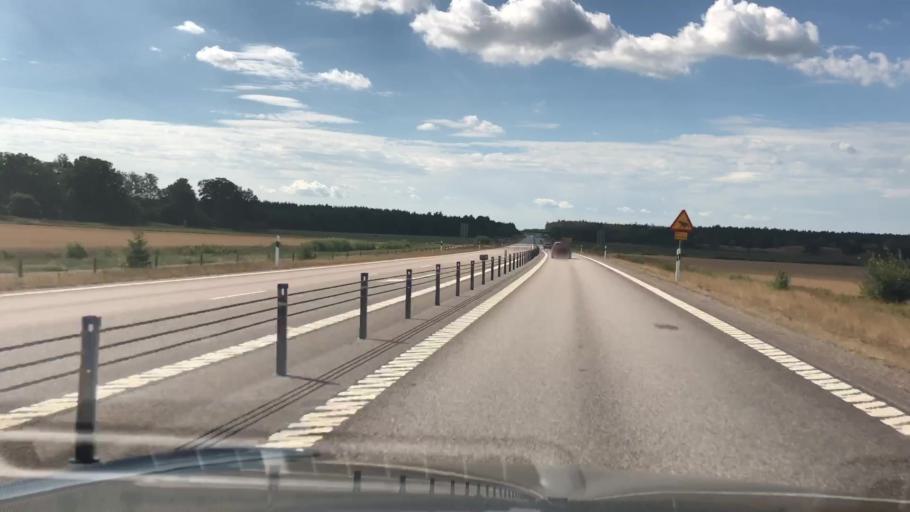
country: SE
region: Kalmar
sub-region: Kalmar Kommun
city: Ljungbyholm
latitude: 56.6091
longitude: 16.1378
